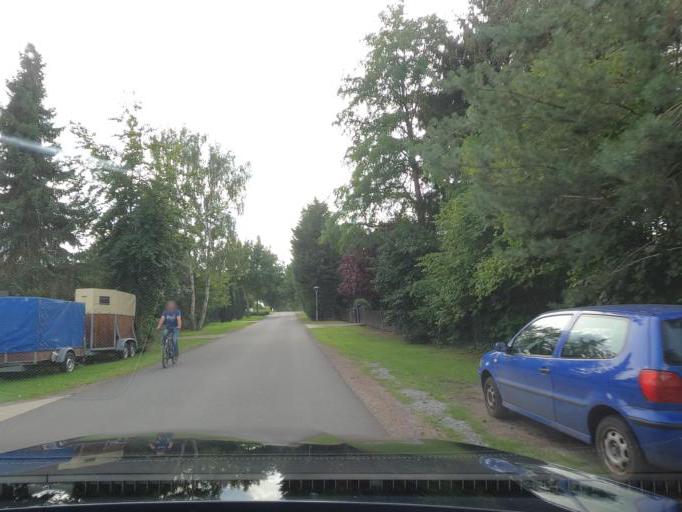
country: DE
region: Lower Saxony
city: Isernhagen Farster Bauerschaft
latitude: 52.5235
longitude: 9.8708
